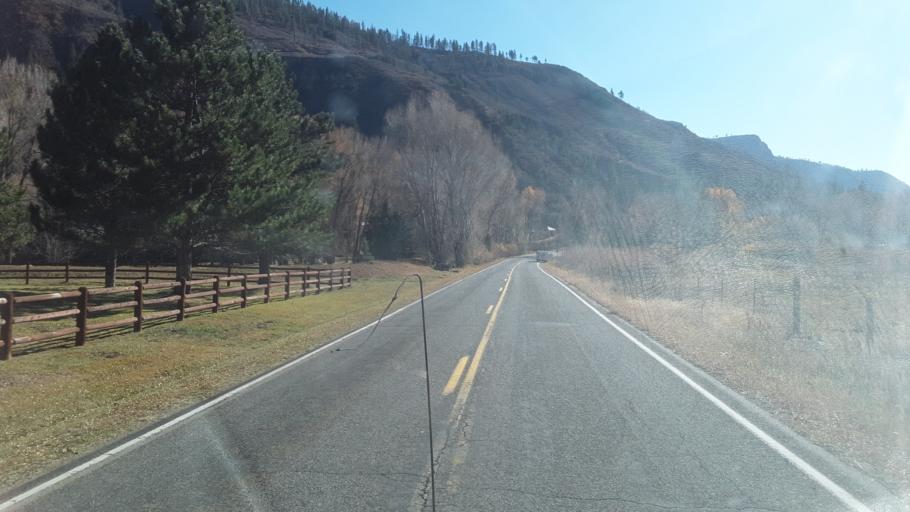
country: US
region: Colorado
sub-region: La Plata County
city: Durango
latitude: 37.4235
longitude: -107.7996
